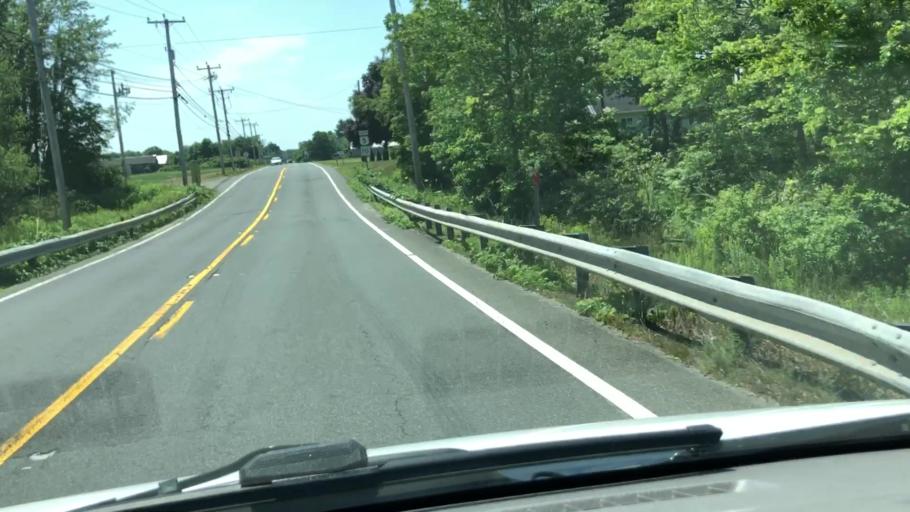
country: US
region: Massachusetts
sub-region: Franklin County
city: Whately
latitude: 42.4445
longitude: -72.6257
